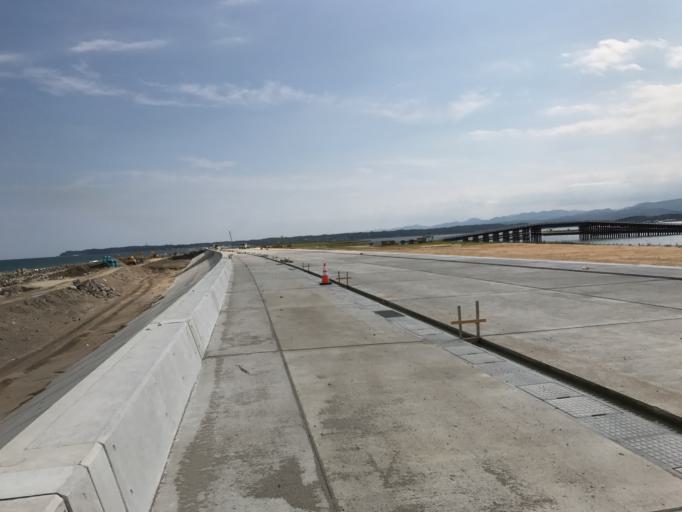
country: JP
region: Miyagi
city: Marumori
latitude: 37.8080
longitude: 140.9855
